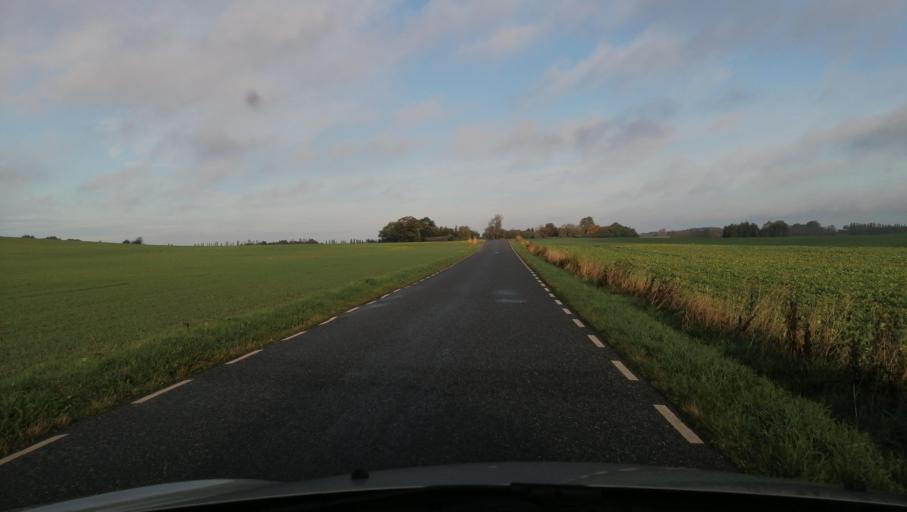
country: DK
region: Zealand
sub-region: Odsherred Kommune
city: Horve
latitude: 55.7468
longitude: 11.3848
